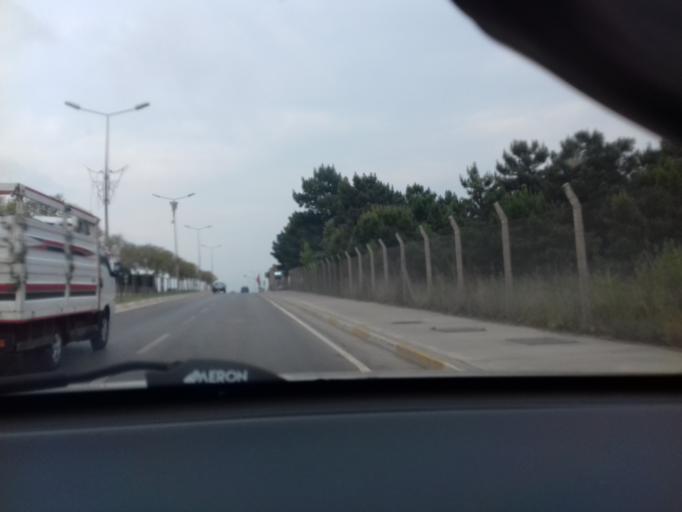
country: TR
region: Istanbul
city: Icmeler
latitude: 40.8832
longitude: 29.3485
